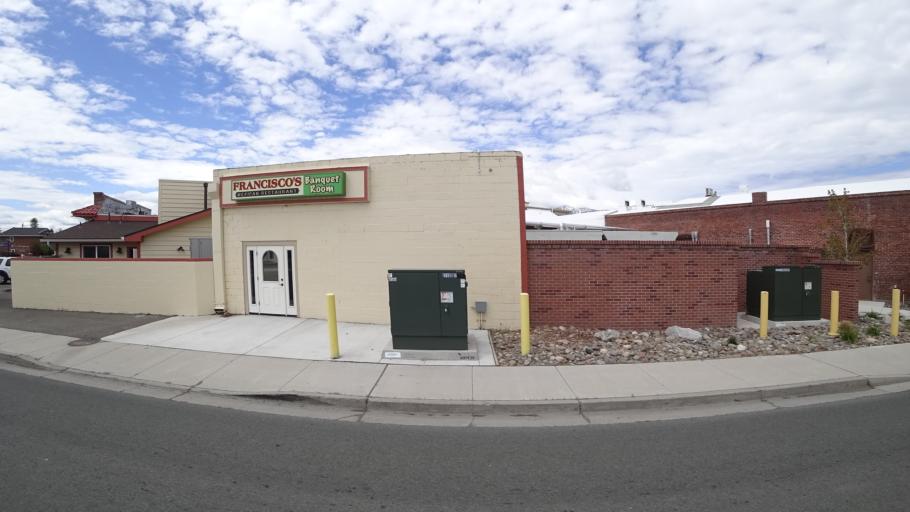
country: US
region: Nevada
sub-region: Douglas County
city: Minden
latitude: 38.9535
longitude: -119.7626
